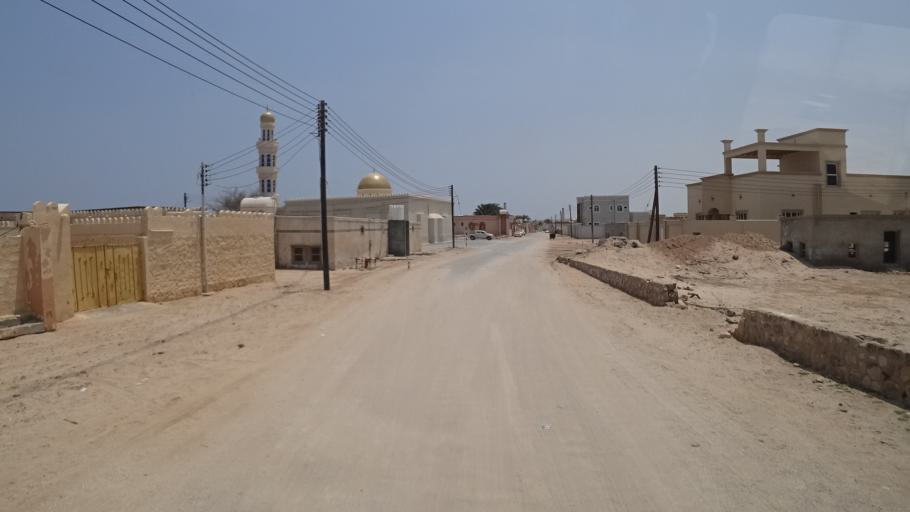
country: OM
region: Ash Sharqiyah
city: Sur
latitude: 22.5160
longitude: 59.7992
